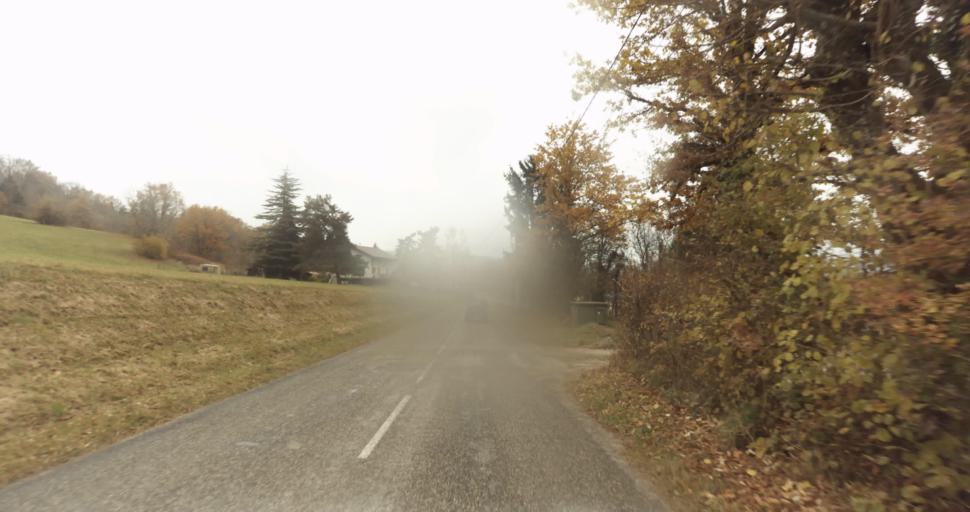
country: FR
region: Rhone-Alpes
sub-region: Departement de la Haute-Savoie
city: Saint-Martin-Bellevue
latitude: 45.9917
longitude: 6.1560
